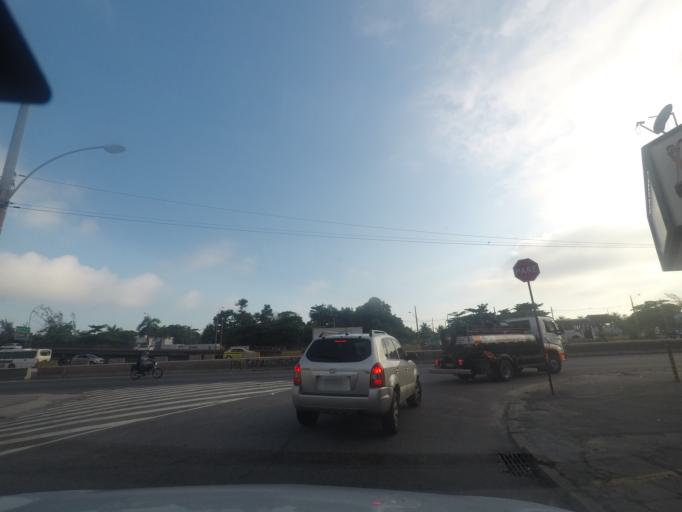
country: BR
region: Rio de Janeiro
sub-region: Duque De Caxias
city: Duque de Caxias
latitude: -22.8282
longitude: -43.2735
